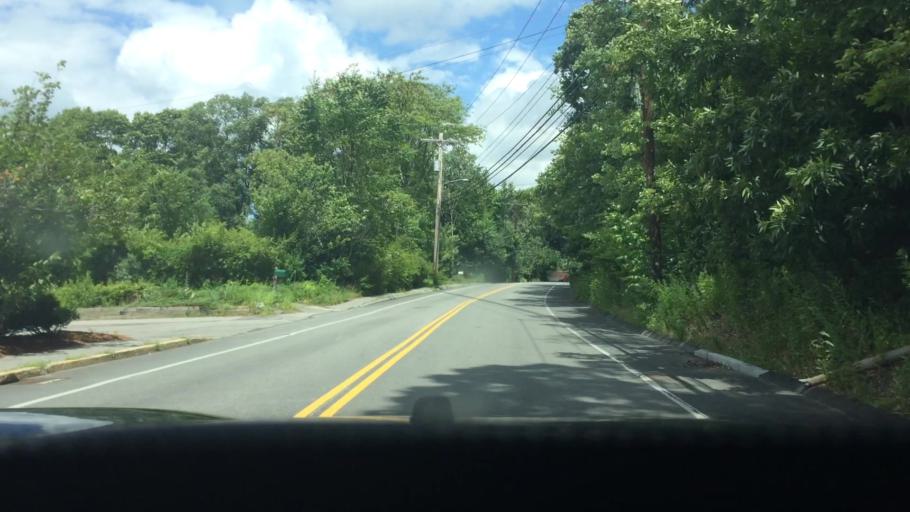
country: US
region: Massachusetts
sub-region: Middlesex County
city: Acton
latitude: 42.4695
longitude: -71.4560
